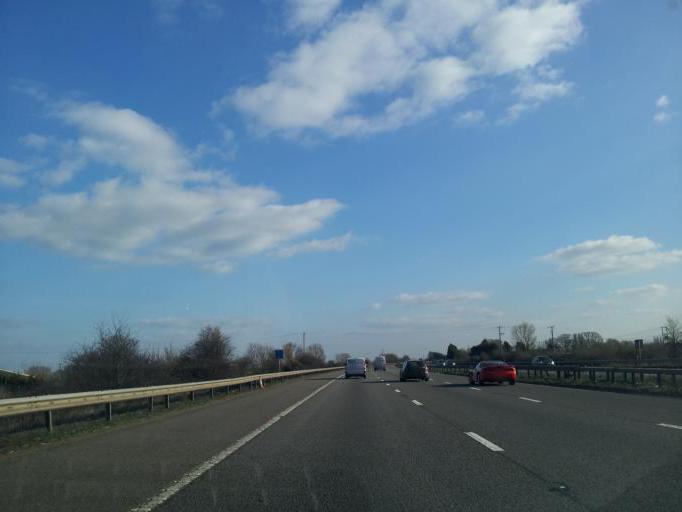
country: GB
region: England
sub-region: Somerset
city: Puriton
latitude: 51.1428
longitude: -2.9729
